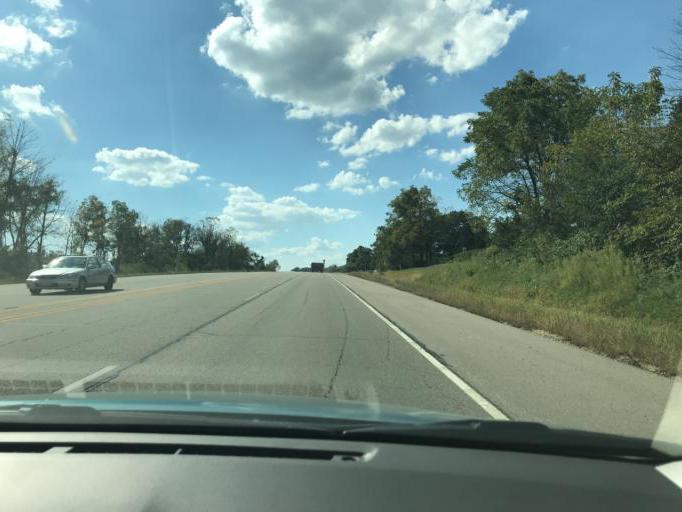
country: US
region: Wisconsin
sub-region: Walworth County
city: Lake Geneva
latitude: 42.5901
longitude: -88.4577
